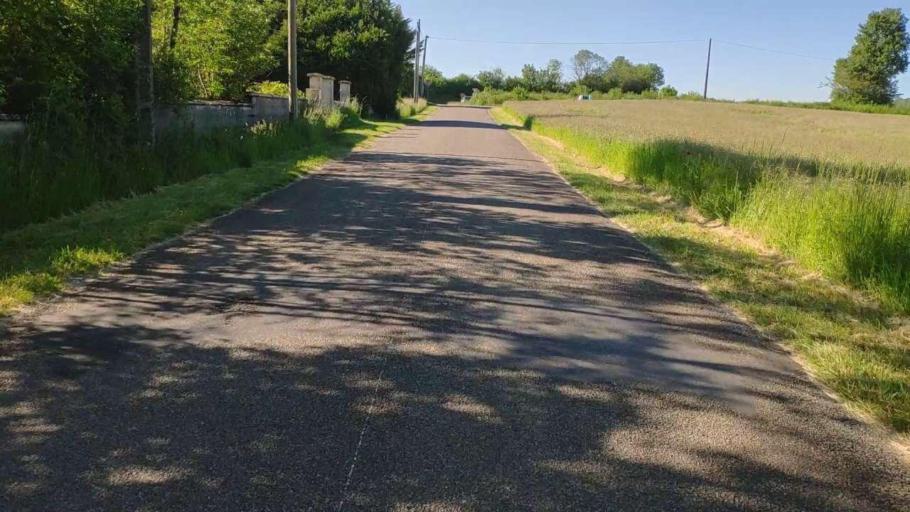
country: FR
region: Franche-Comte
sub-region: Departement du Jura
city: Perrigny
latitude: 46.6865
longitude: 5.6385
